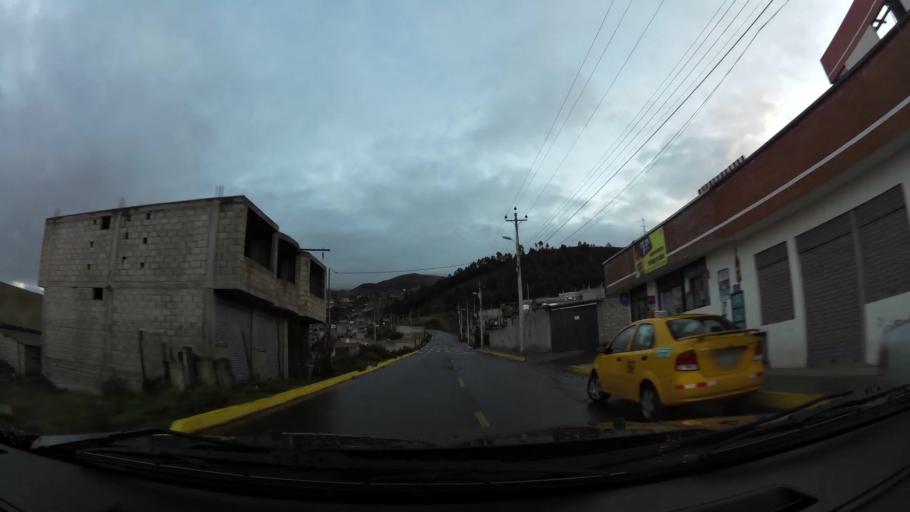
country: EC
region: Pichincha
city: Quito
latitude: -0.0912
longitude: -78.5293
